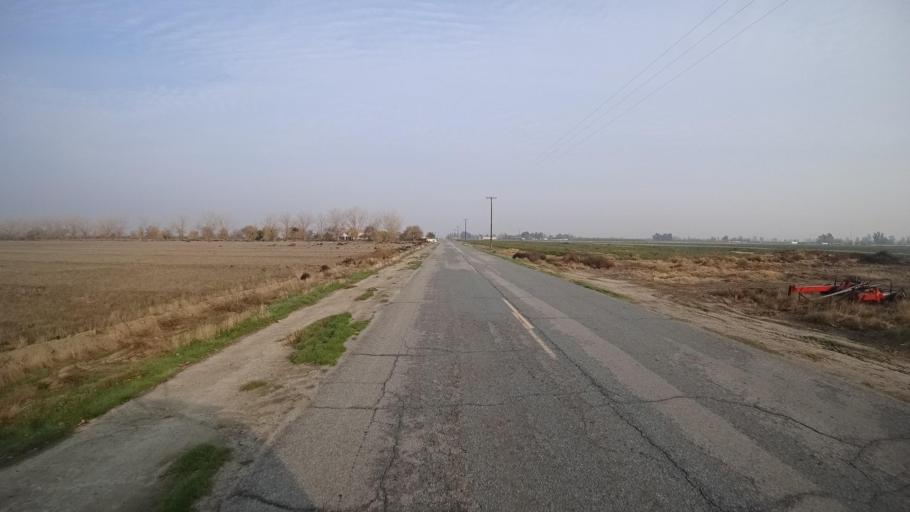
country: US
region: California
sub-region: Kern County
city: Greenfield
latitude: 35.2125
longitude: -119.0215
